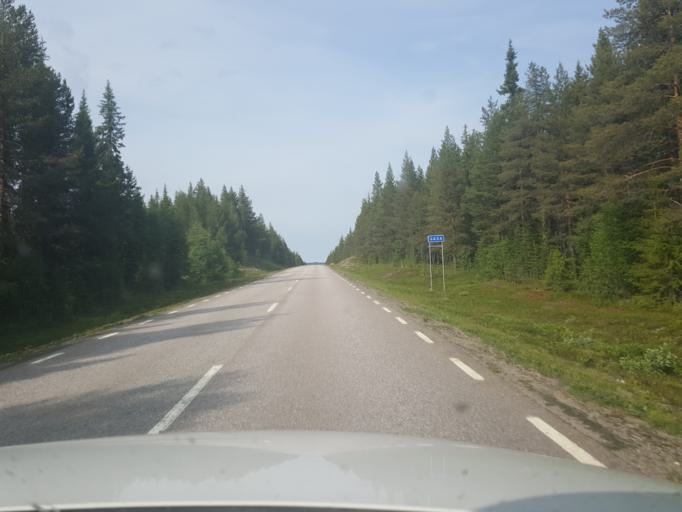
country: SE
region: Norrbotten
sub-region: Arjeplogs Kommun
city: Arjeplog
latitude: 65.6936
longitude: 18.0678
